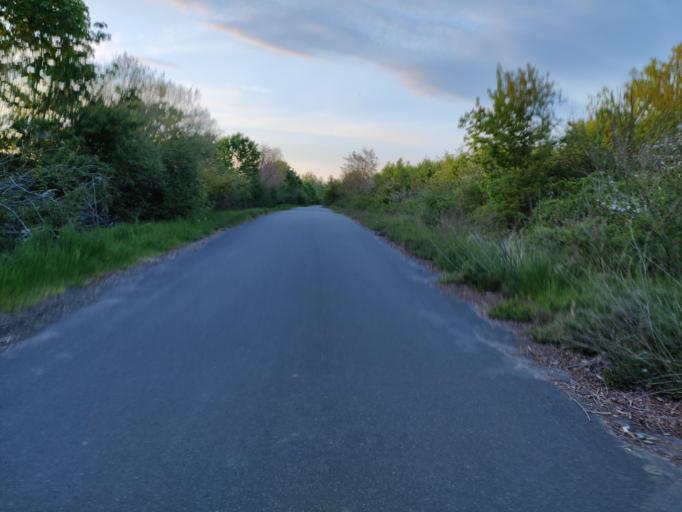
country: DE
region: Saxony
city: Markkleeberg
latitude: 51.2403
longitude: 12.3668
